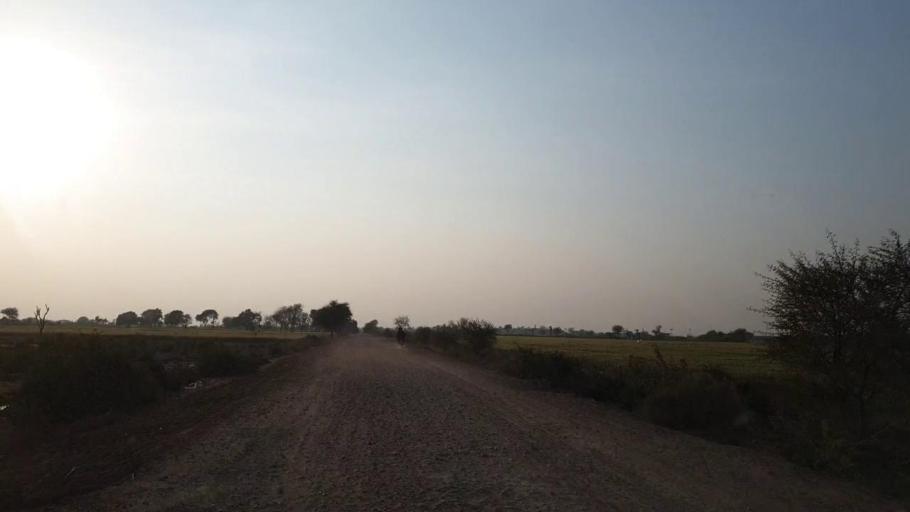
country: PK
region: Sindh
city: Pithoro
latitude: 25.6541
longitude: 69.2283
